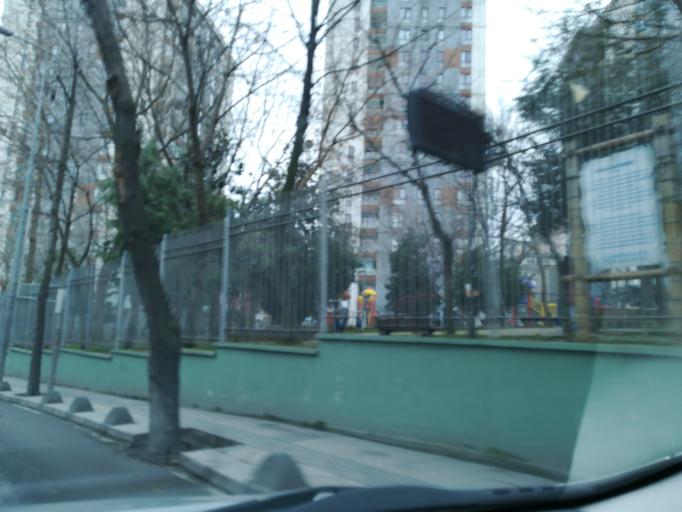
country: TR
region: Istanbul
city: Mahmutbey
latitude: 41.0447
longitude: 28.8337
